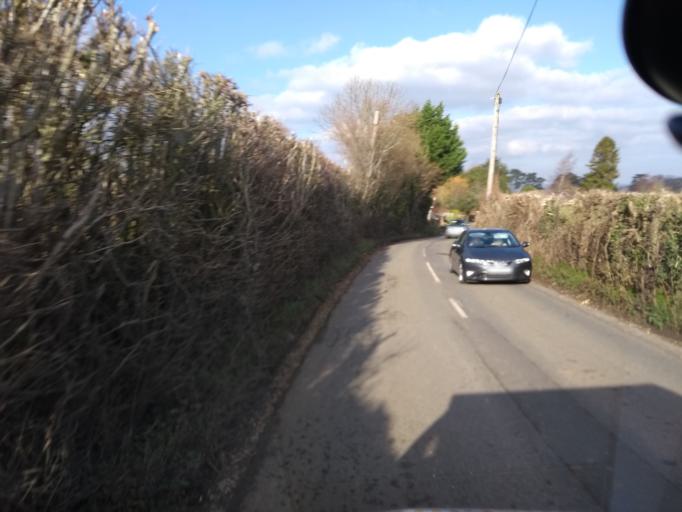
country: GB
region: England
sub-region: Somerset
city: Creech Saint Michael
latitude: 50.9763
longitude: -3.0556
